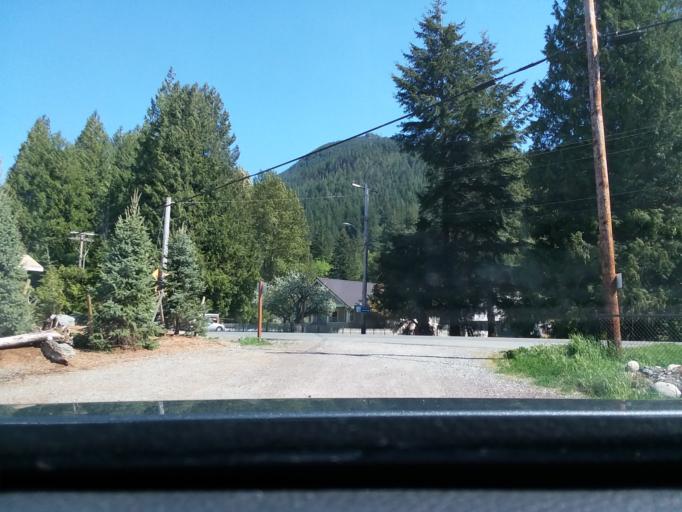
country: US
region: Washington
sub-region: Snohomish County
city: Gold Bar
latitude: 47.7082
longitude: -121.3593
